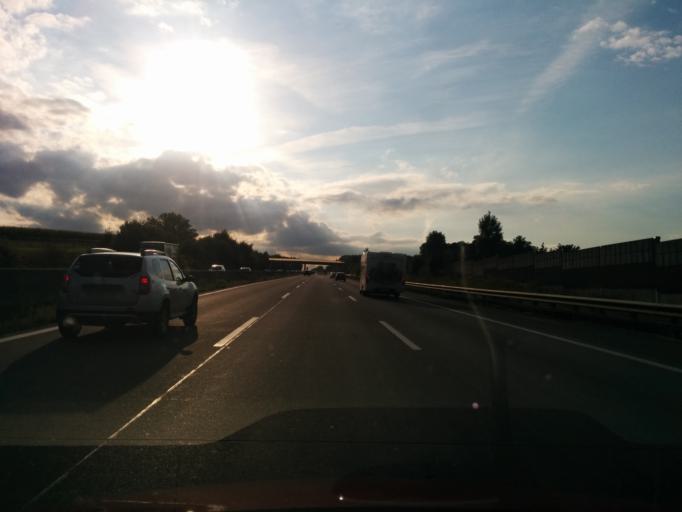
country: AT
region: Lower Austria
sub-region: Politischer Bezirk Melk
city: Blindenmarkt
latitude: 48.1372
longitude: 14.9746
